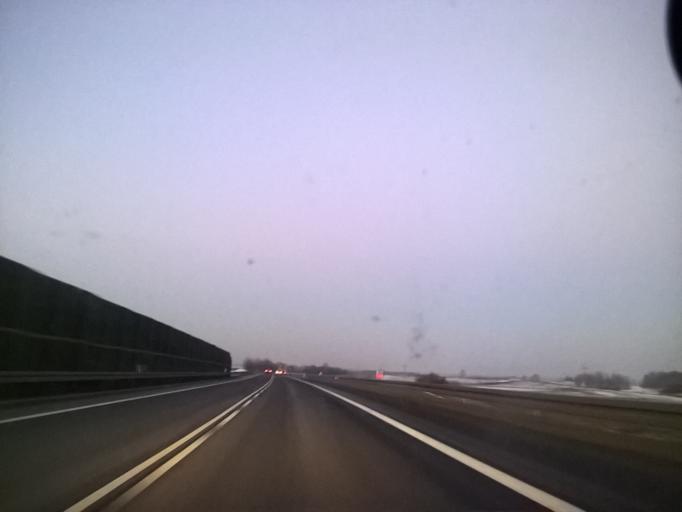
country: PL
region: Warmian-Masurian Voivodeship
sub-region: Powiat olsztynski
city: Biskupiec
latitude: 53.8366
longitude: 20.9278
